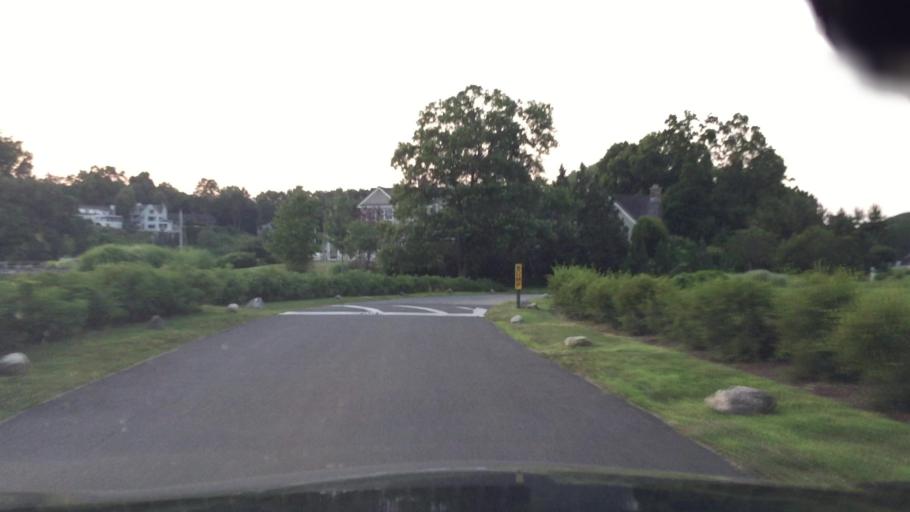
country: US
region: Connecticut
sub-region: Fairfield County
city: Darien
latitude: 41.0671
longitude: -73.4302
